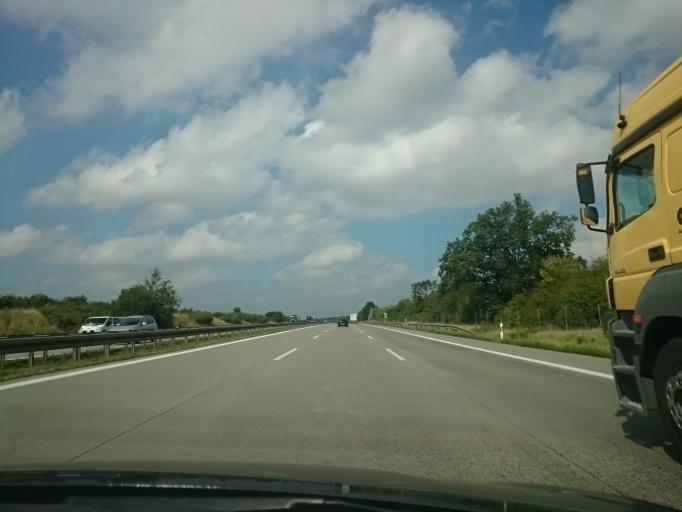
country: DE
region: Berlin
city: Hellersdorf
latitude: 52.5725
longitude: 13.6447
